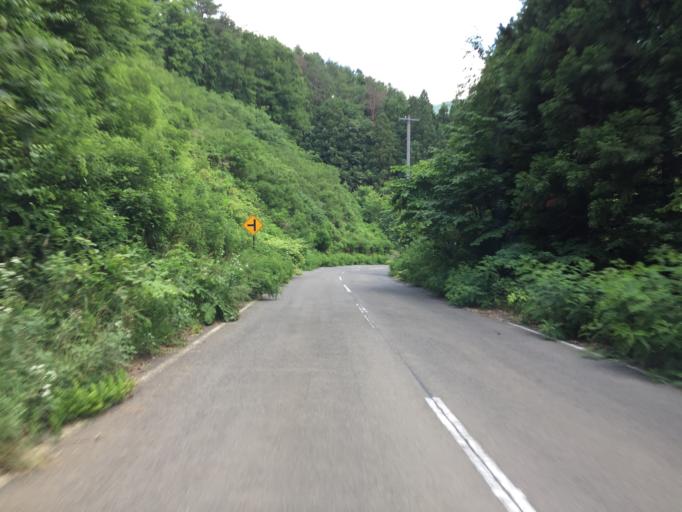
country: JP
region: Fukushima
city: Yanagawamachi-saiwaicho
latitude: 37.7572
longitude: 140.6865
